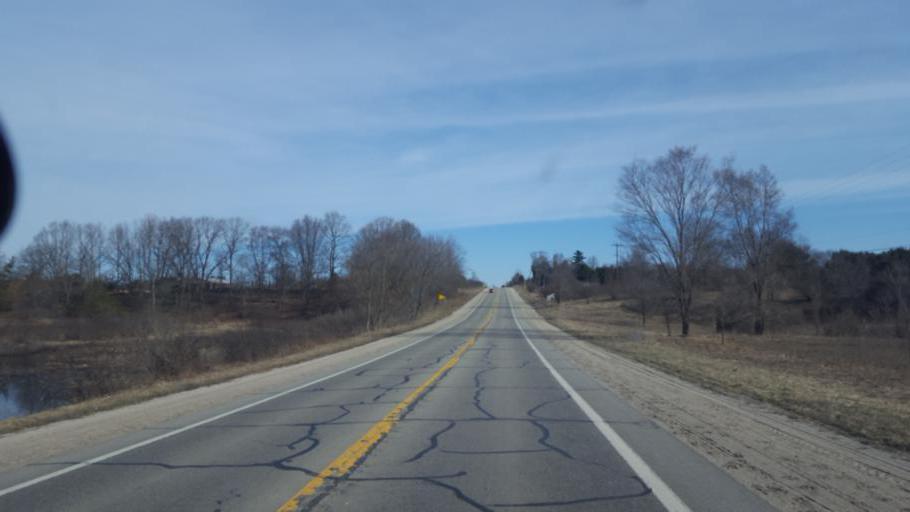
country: US
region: Michigan
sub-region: Montcalm County
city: Howard City
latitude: 43.5061
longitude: -85.4432
